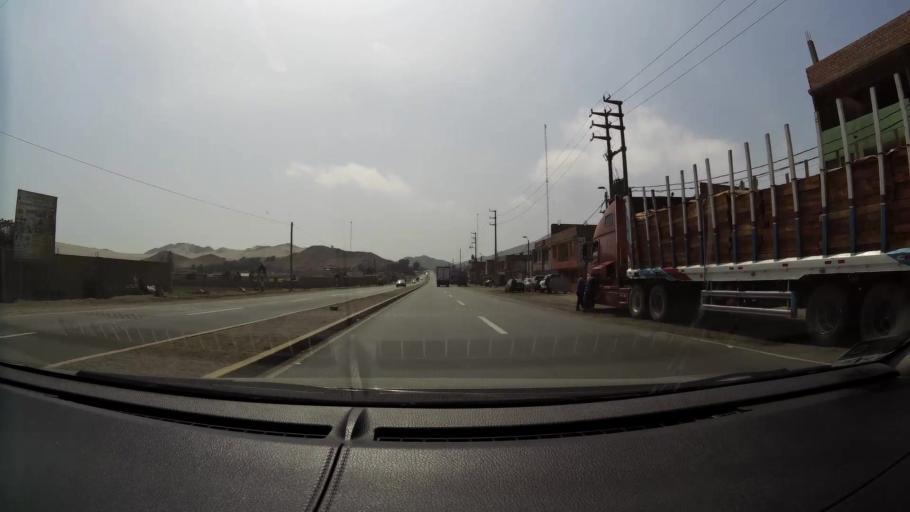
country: PE
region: Lima
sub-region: Provincia de Huaral
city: Chancay
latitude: -11.4881
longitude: -77.3051
